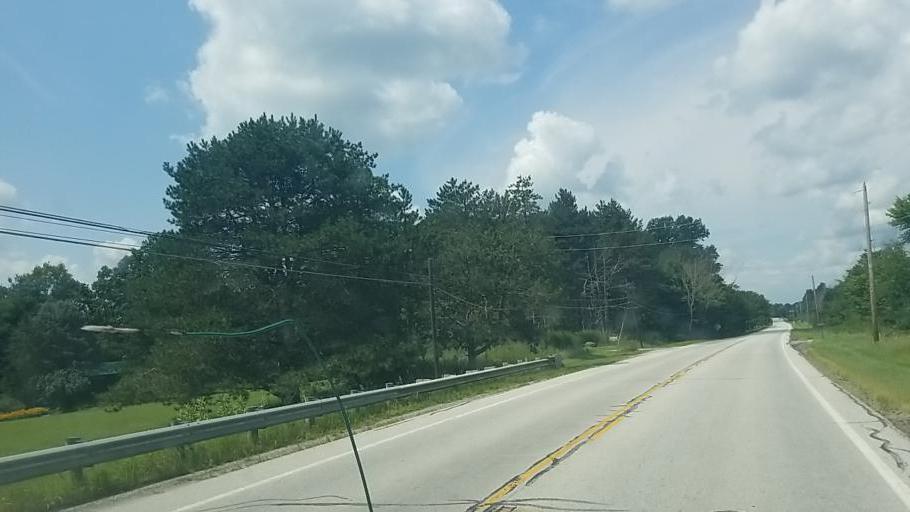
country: US
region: Ohio
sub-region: Wayne County
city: West Salem
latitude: 41.0261
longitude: -82.0782
